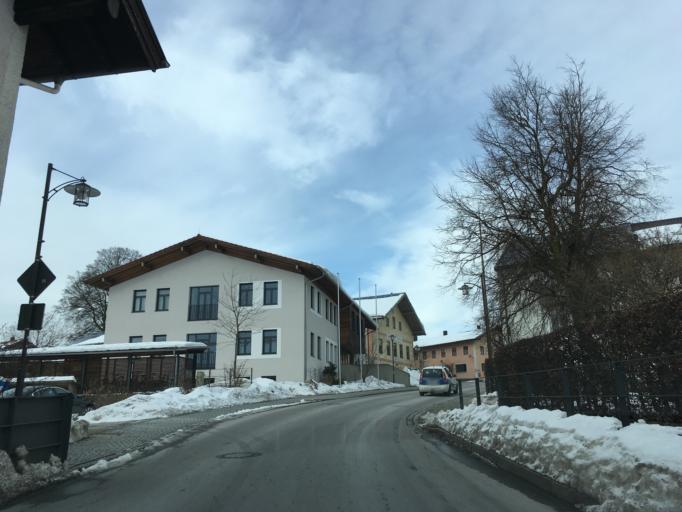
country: DE
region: Bavaria
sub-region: Upper Bavaria
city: Schnaitsee
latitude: 48.0706
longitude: 12.3711
